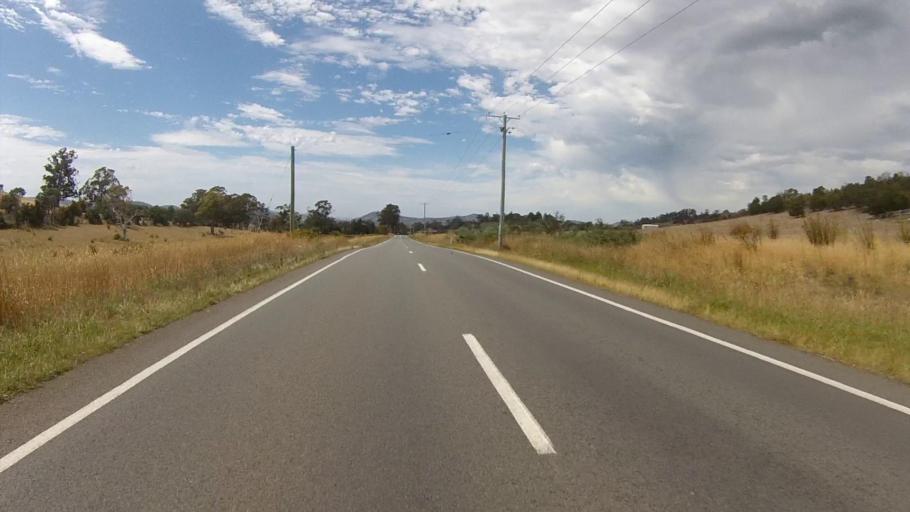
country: AU
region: Tasmania
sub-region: Brighton
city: Old Beach
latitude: -42.6725
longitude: 147.3936
